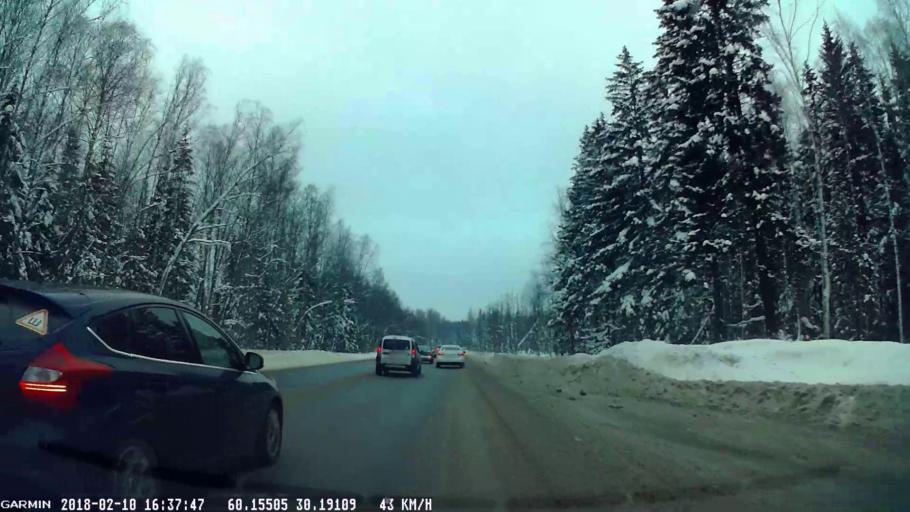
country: RU
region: Leningrad
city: Sertolovo
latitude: 60.1516
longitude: 30.1955
